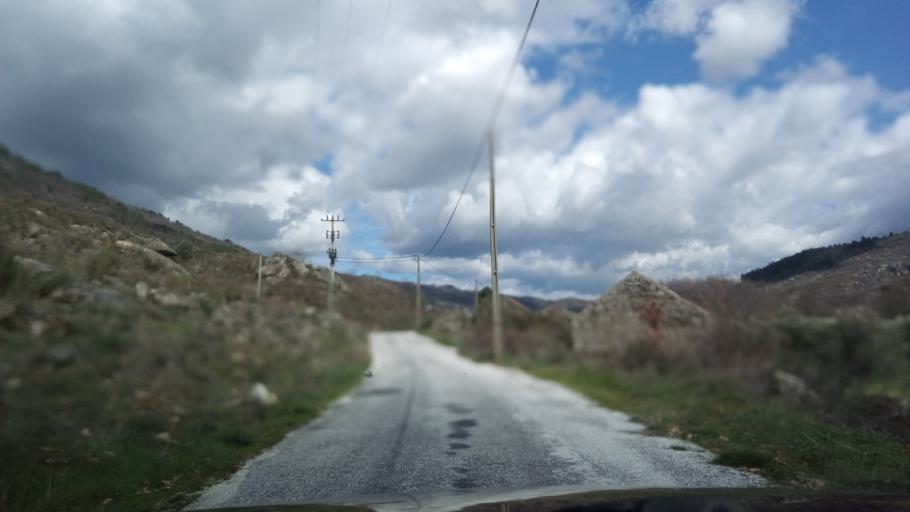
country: PT
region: Guarda
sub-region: Fornos de Algodres
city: Fornos de Algodres
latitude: 40.6422
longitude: -7.5082
